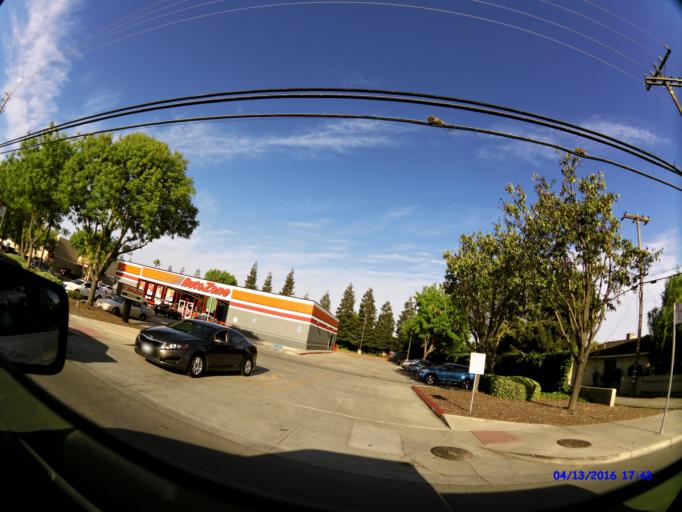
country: US
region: California
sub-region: Stanislaus County
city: Modesto
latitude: 37.6569
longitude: -120.9574
